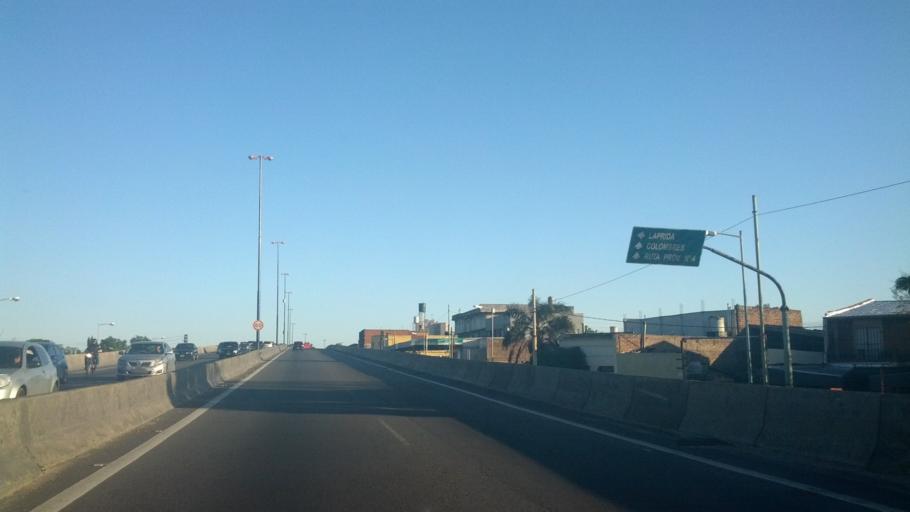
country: AR
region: Buenos Aires
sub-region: Partido de Lomas de Zamora
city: Lomas de Zamora
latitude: -34.7545
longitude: -58.4343
